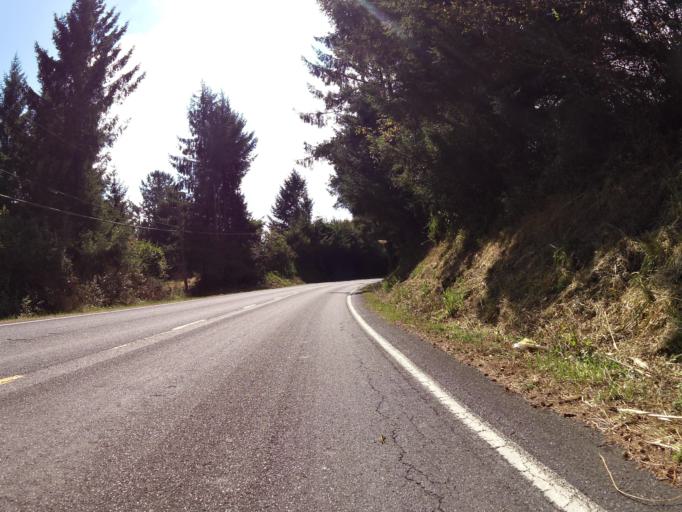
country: US
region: California
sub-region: Humboldt County
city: Humboldt Hill
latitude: 40.6526
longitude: -124.2209
